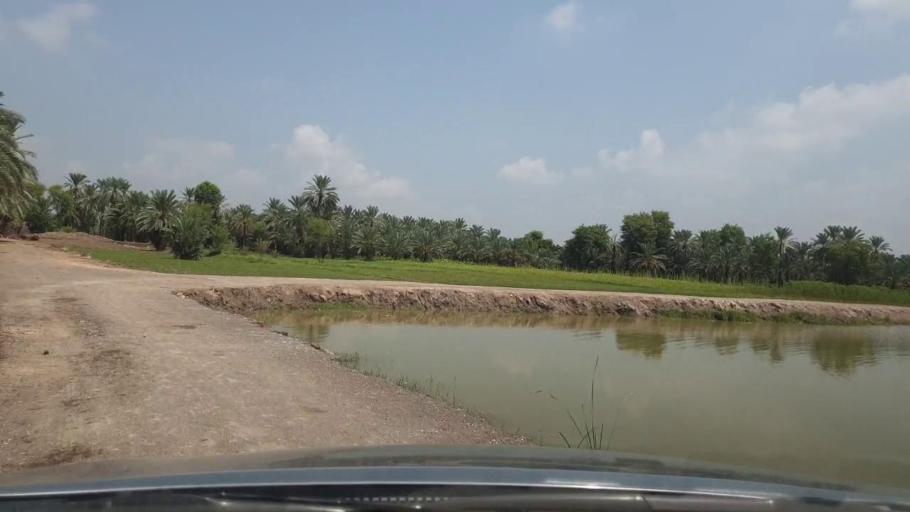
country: PK
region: Sindh
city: Pir jo Goth
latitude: 27.6200
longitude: 68.6642
